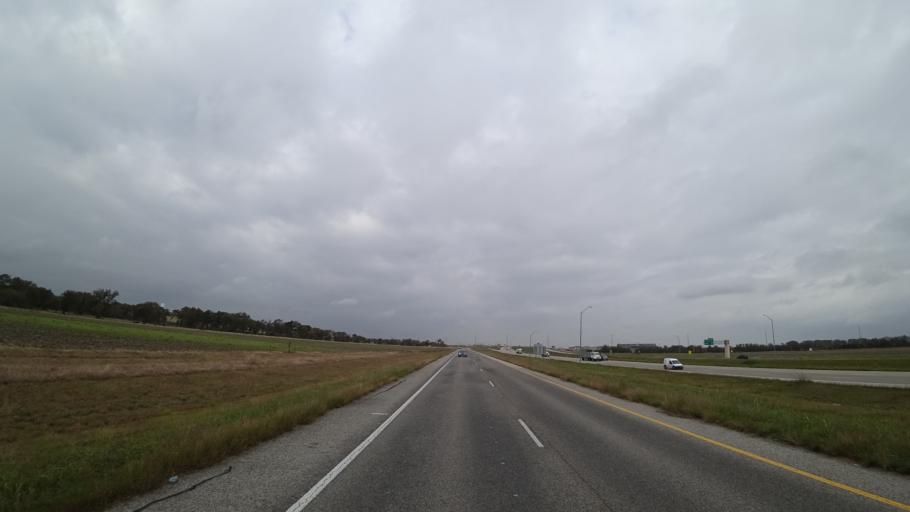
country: US
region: Texas
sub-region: Travis County
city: Pflugerville
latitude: 30.4428
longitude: -97.5937
